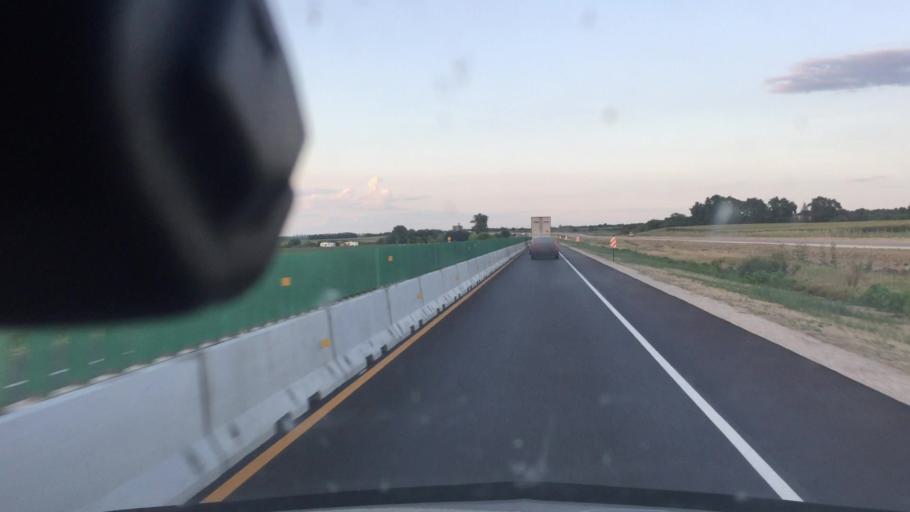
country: US
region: Illinois
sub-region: Livingston County
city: Pontiac
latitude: 40.9429
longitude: -88.5905
